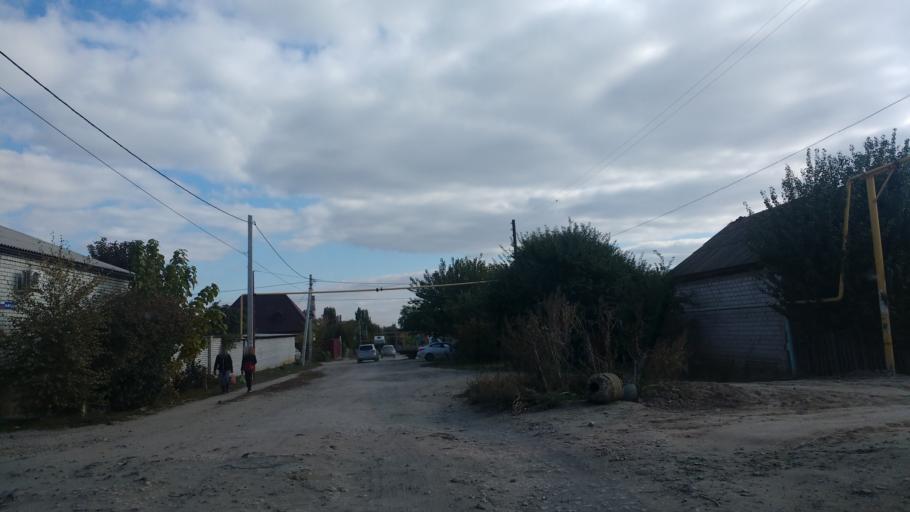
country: RU
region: Volgograd
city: Volgograd
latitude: 48.7570
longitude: 44.5426
